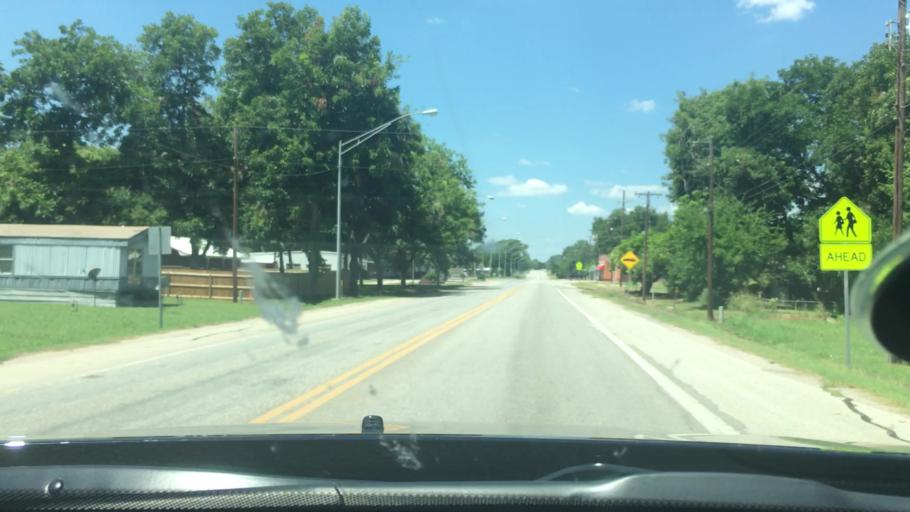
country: US
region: Oklahoma
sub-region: Carter County
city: Dickson
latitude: 34.1863
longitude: -96.8784
